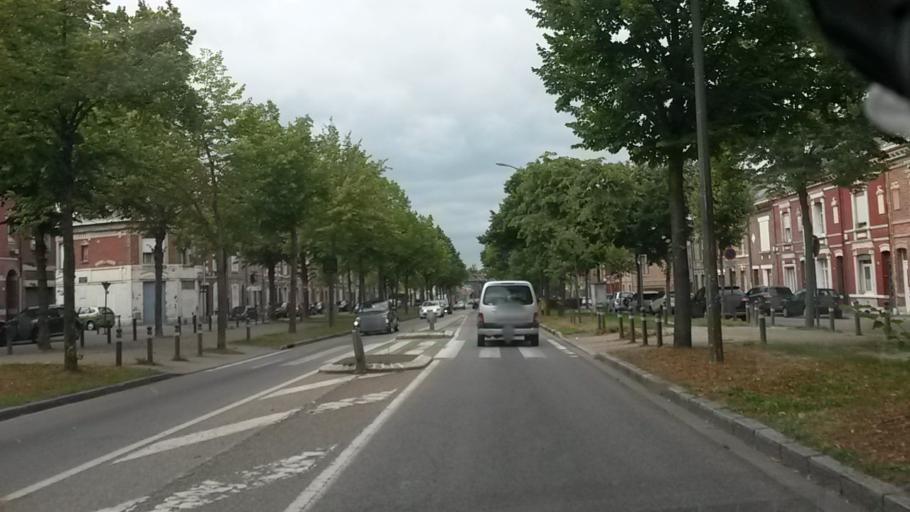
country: FR
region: Picardie
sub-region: Departement de la Somme
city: Amiens
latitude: 49.8851
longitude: 2.2806
